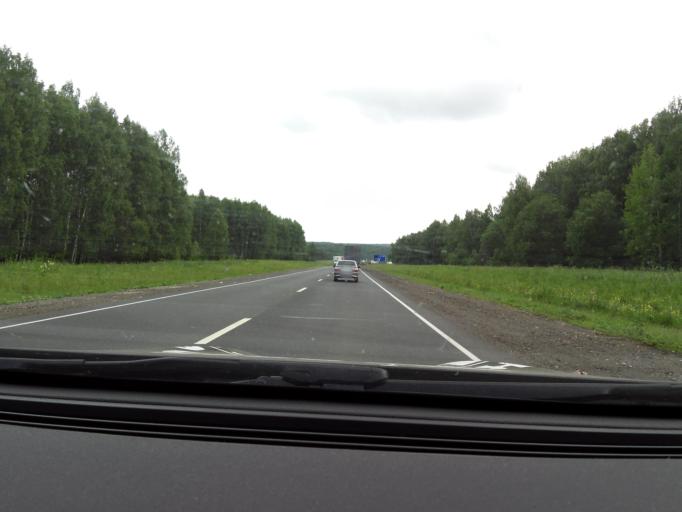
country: RU
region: Perm
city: Suksun
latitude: 57.1472
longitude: 57.2850
